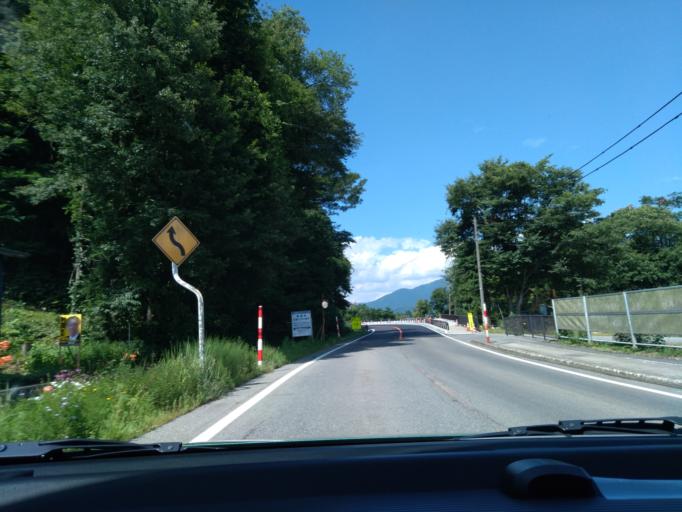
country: JP
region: Akita
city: Kakunodatemachi
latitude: 39.6837
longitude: 140.7072
